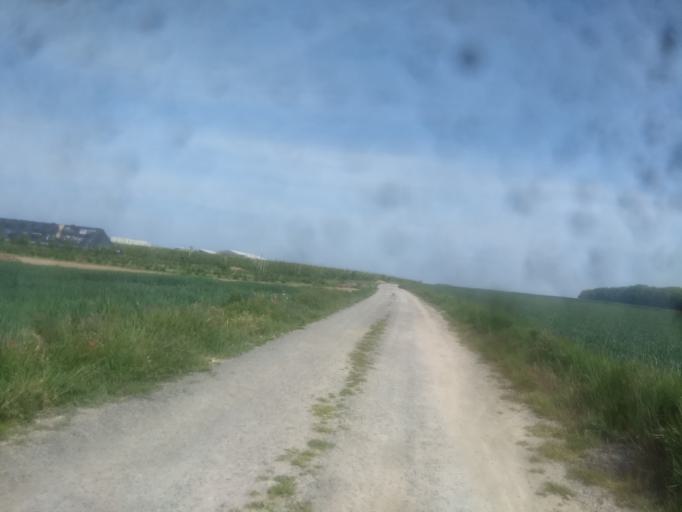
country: FR
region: Nord-Pas-de-Calais
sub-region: Departement du Pas-de-Calais
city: Beaurains
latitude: 50.2606
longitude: 2.8076
